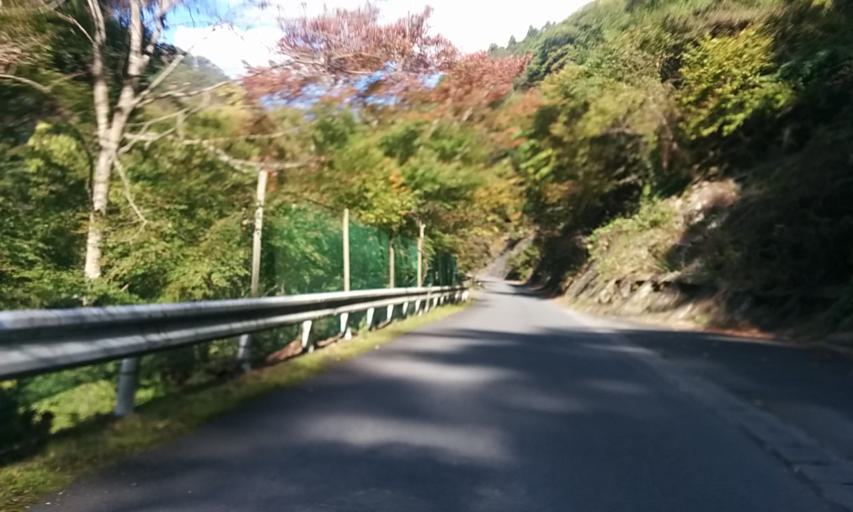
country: JP
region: Kyoto
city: Kameoka
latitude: 35.1331
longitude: 135.5758
